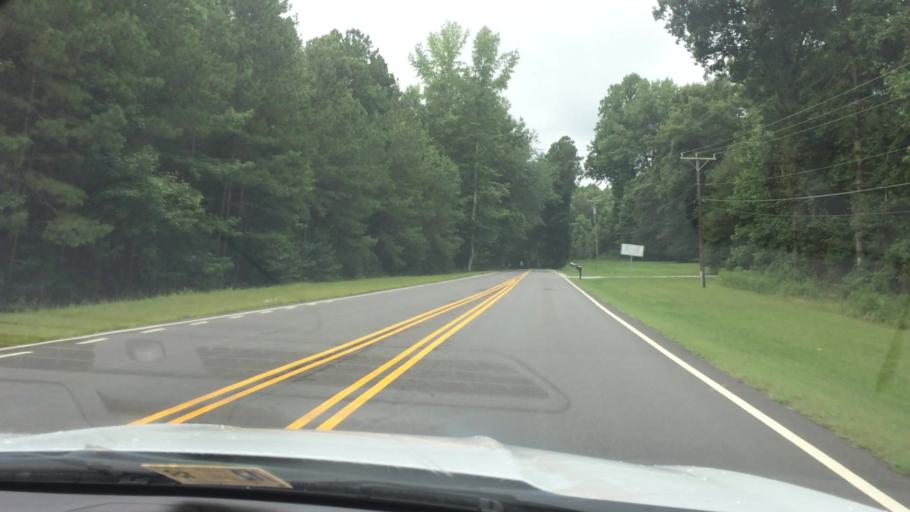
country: US
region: Virginia
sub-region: New Kent County
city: New Kent
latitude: 37.4642
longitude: -77.0344
